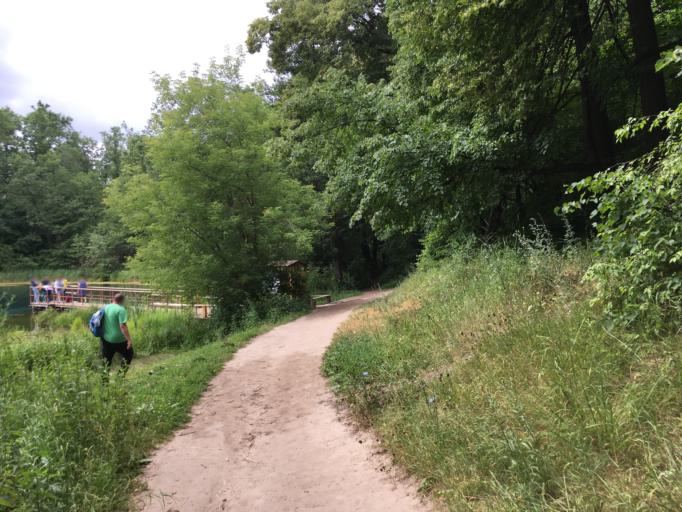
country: RU
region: Tatarstan
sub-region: Gorod Kazan'
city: Kazan
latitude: 55.9071
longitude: 49.1551
